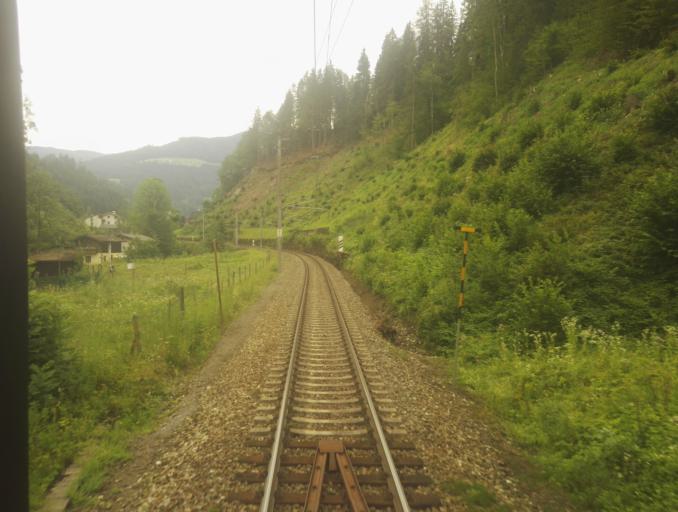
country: AT
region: Salzburg
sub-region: Politischer Bezirk Sankt Johann im Pongau
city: Huttau
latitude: 47.4198
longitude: 13.3002
